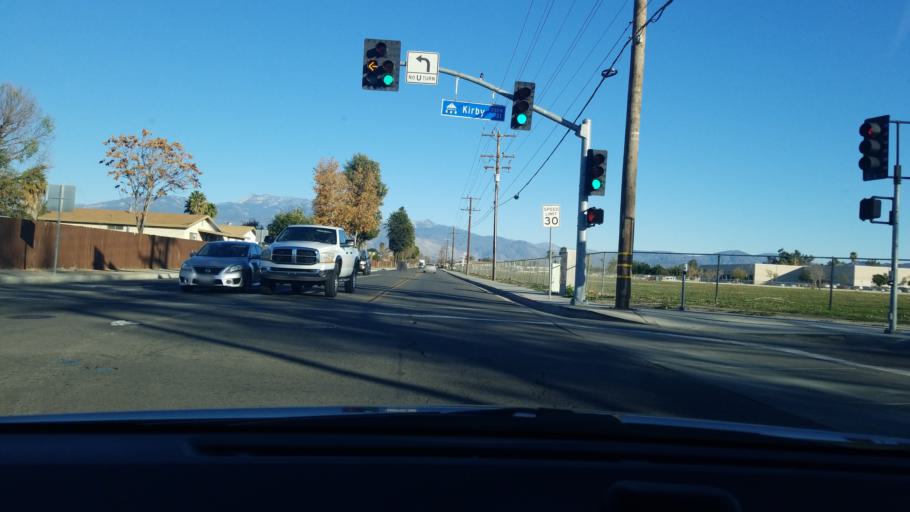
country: US
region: California
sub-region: Riverside County
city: Hemet
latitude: 33.7510
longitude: -116.9979
